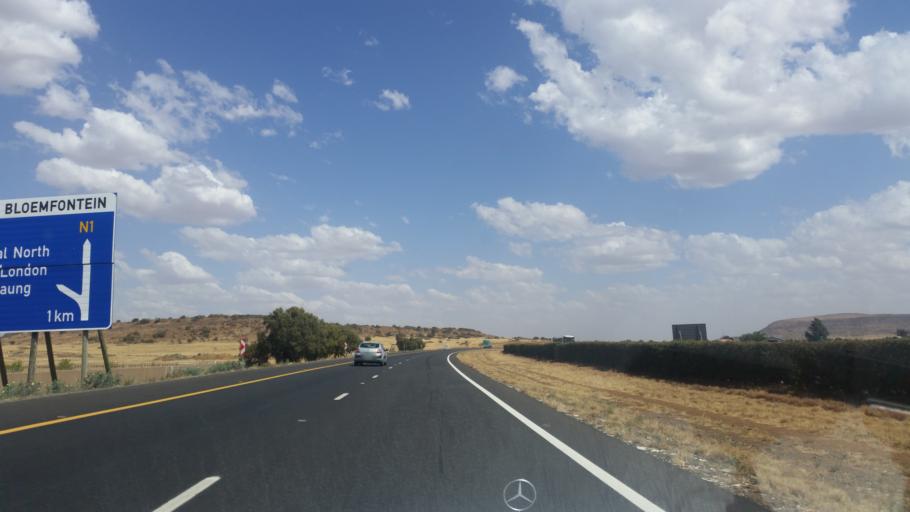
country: ZA
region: Orange Free State
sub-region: Mangaung Metropolitan Municipality
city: Bloemfontein
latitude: -29.1882
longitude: 26.1934
